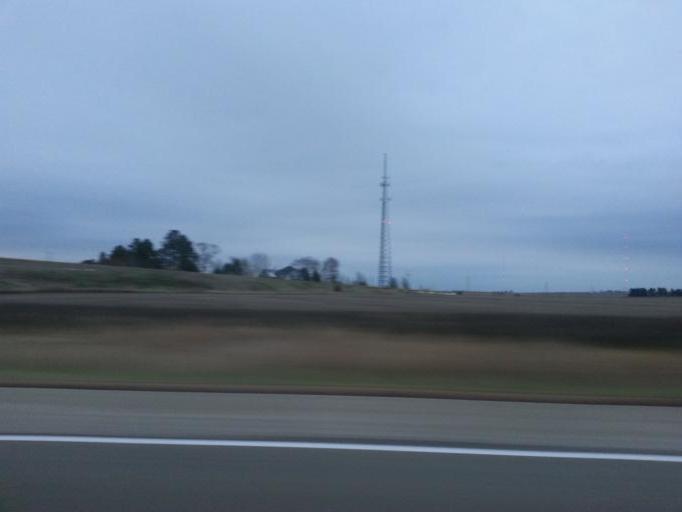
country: US
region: Iowa
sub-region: Benton County
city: Urbana
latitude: 42.2813
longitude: -91.9399
